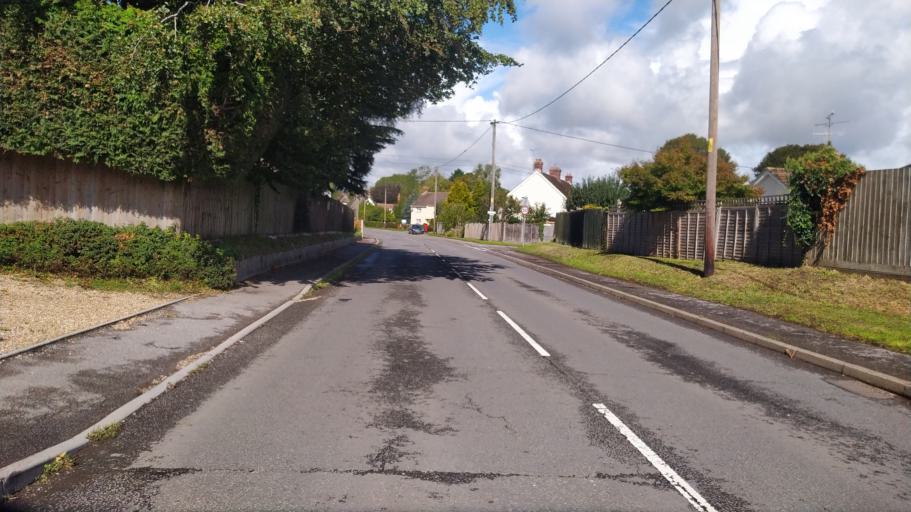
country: GB
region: England
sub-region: Dorset
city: Manston
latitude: 50.8957
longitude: -2.2434
